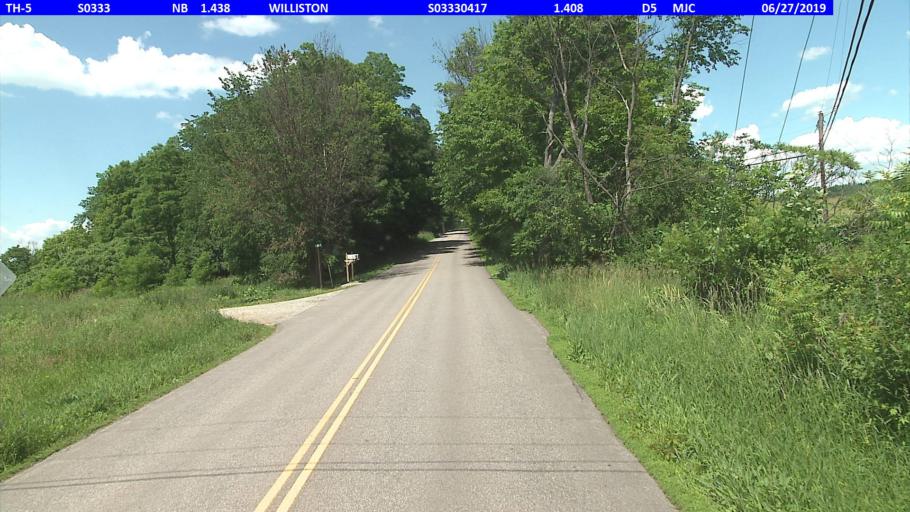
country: US
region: Vermont
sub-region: Chittenden County
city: South Burlington
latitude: 44.4214
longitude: -73.1357
